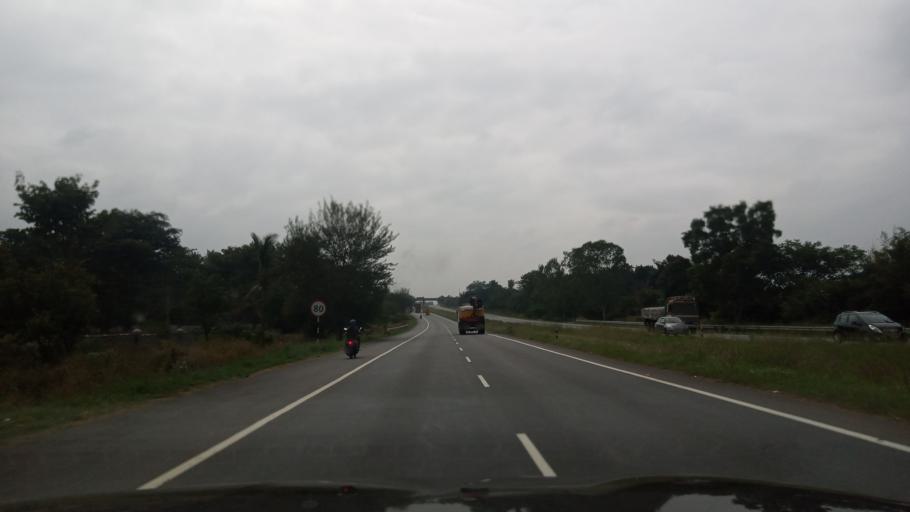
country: IN
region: Karnataka
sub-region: Bangalore Urban
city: Bangalore
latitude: 12.9323
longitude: 77.4695
